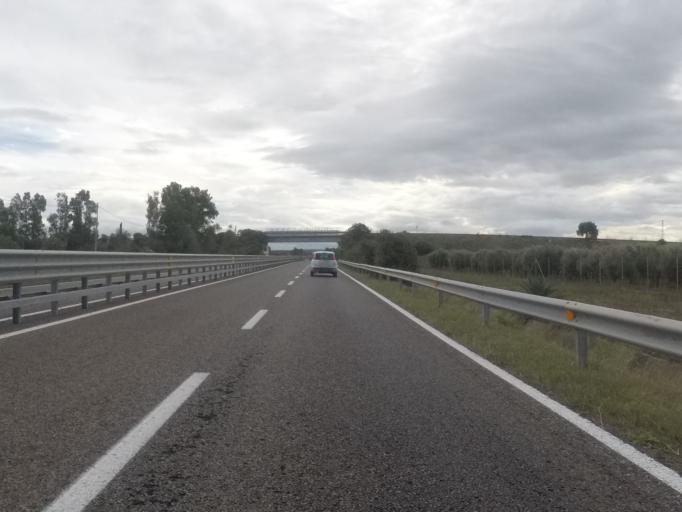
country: IT
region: Sardinia
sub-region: Provincia di Cagliari
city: Villaspeciosa
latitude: 39.3071
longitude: 8.9155
